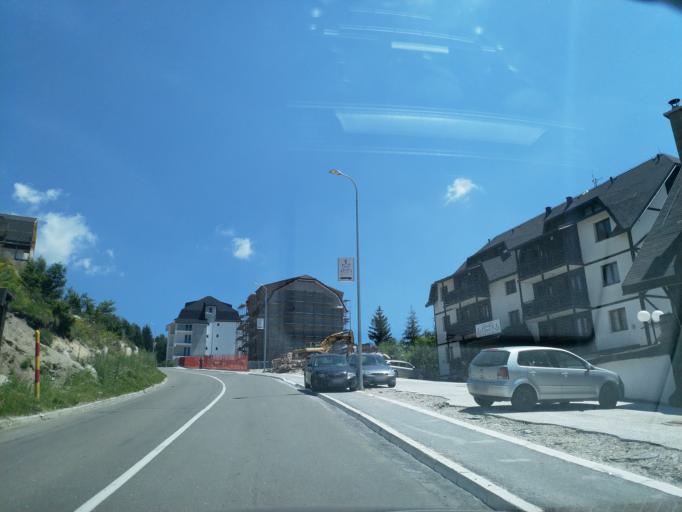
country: RS
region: Central Serbia
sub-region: Raski Okrug
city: Raska
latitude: 43.2757
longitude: 20.7600
